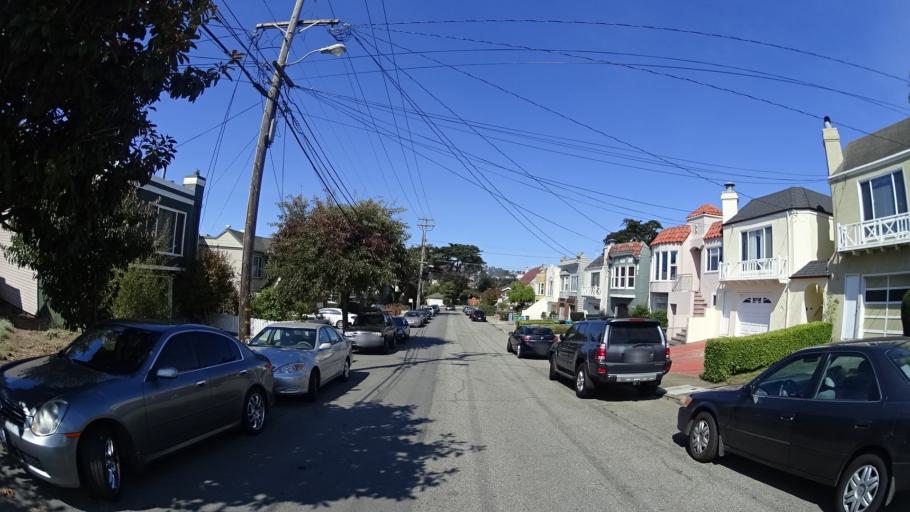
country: US
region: California
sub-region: San Mateo County
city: Daly City
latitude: 37.7208
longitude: -122.4681
